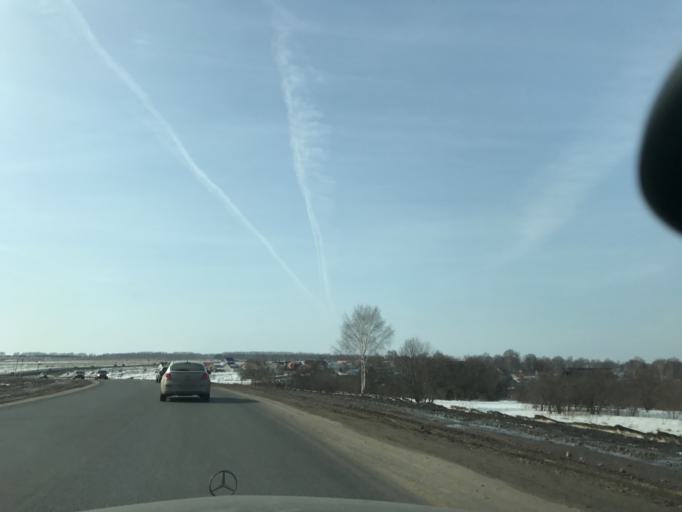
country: RU
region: Nizjnij Novgorod
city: Bogorodsk
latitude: 56.0883
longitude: 43.5124
